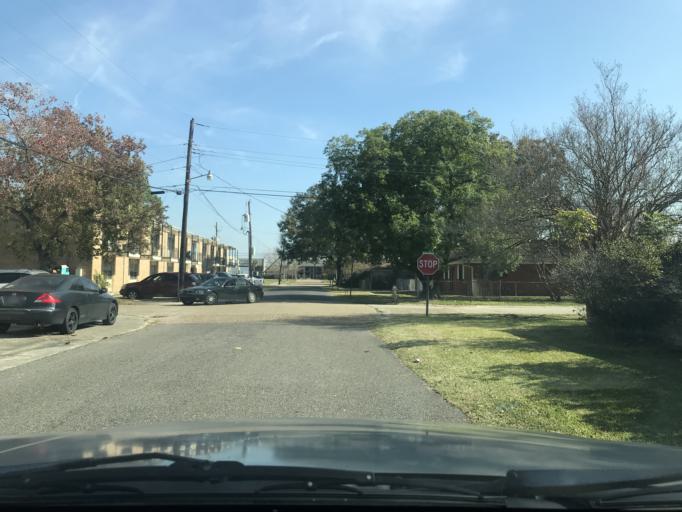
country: US
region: Louisiana
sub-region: Jefferson Parish
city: Marrero
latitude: 29.8944
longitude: -90.0908
